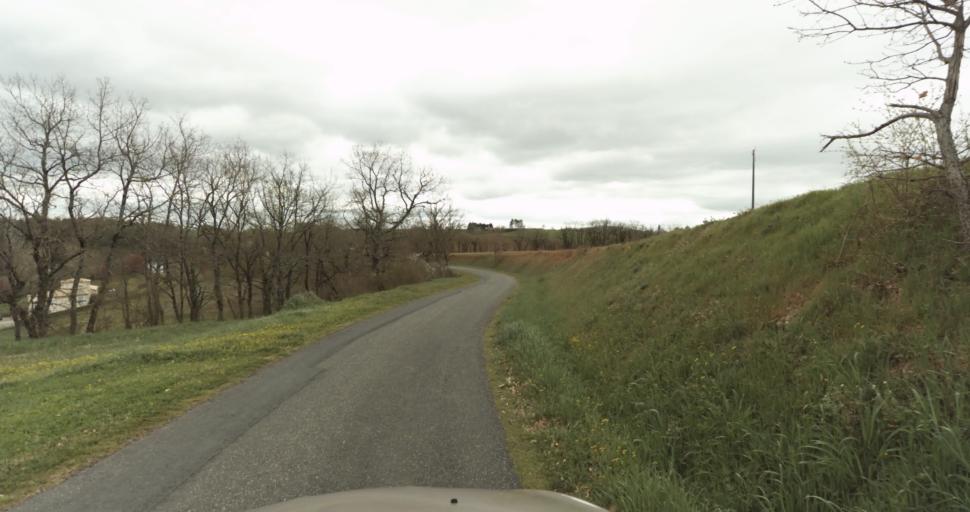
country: FR
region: Midi-Pyrenees
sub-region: Departement du Tarn
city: Puygouzon
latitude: 43.8704
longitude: 2.1696
